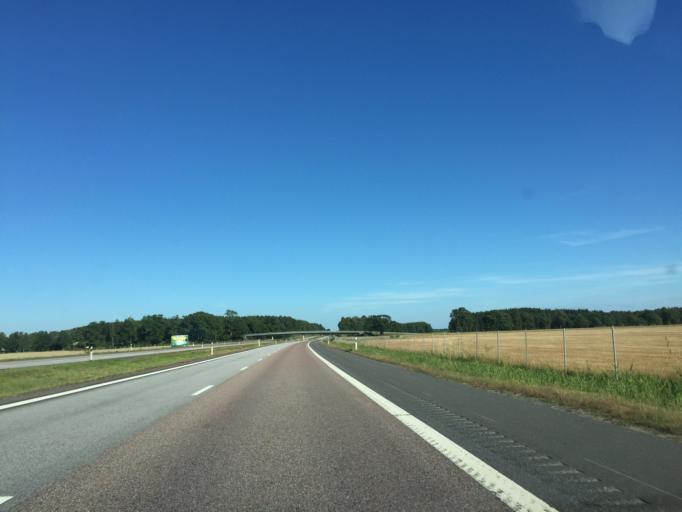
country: SE
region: OErebro
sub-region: Orebro Kommun
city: Hovsta
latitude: 59.3069
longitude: 15.3302
